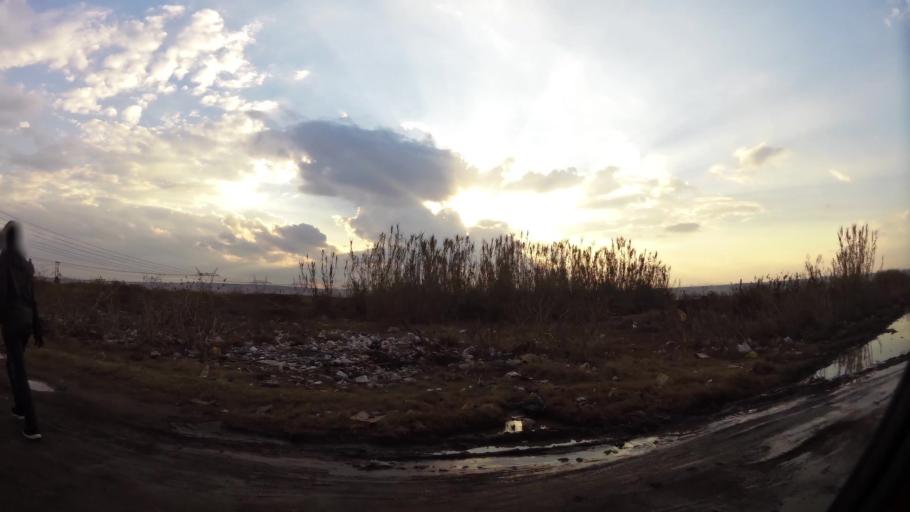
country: ZA
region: Gauteng
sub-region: City of Johannesburg Metropolitan Municipality
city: Orange Farm
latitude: -26.5511
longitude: 27.8322
